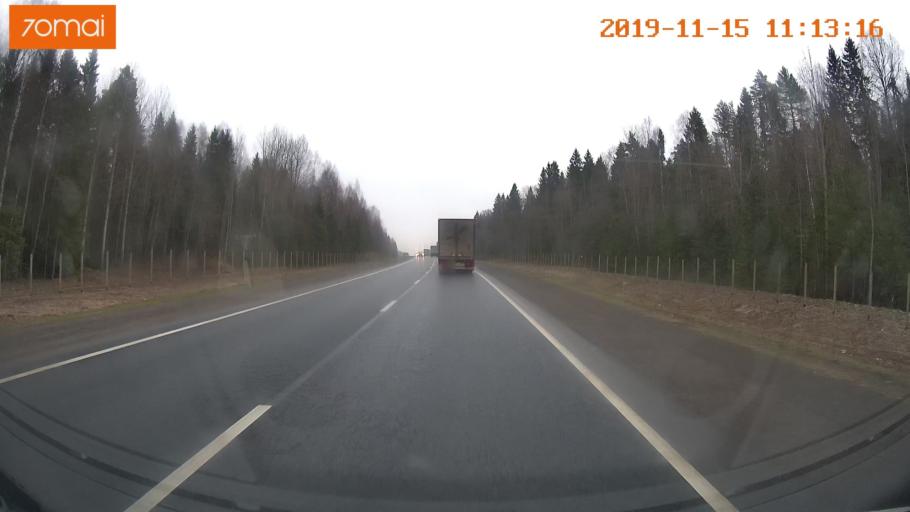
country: RU
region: Vologda
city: Chebsara
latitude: 59.1219
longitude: 39.1653
